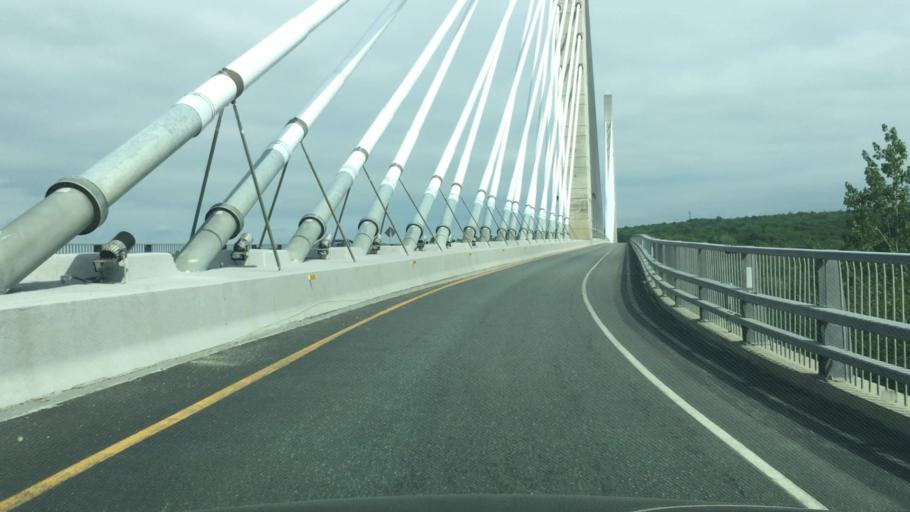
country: US
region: Maine
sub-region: Hancock County
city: Bucksport
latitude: 44.5610
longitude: -68.8055
